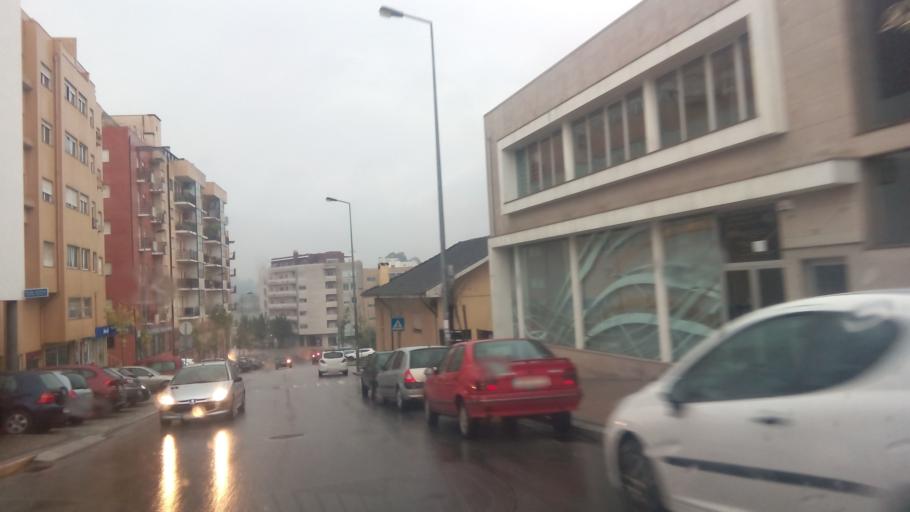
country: PT
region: Porto
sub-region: Paredes
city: Paredes
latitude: 41.2079
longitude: -8.3308
